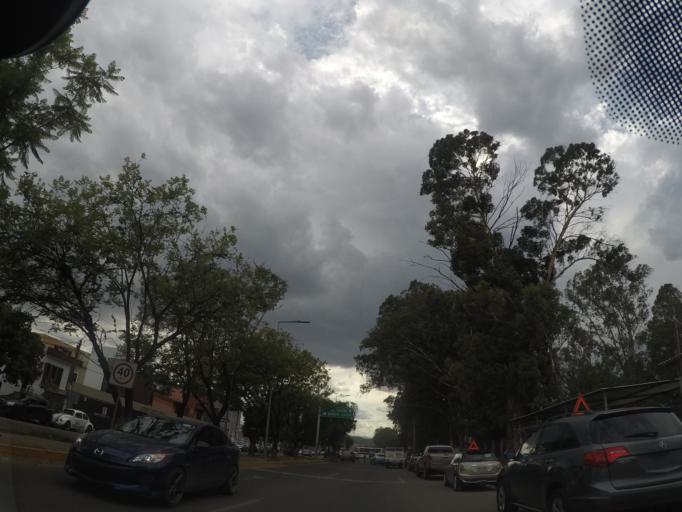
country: MX
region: Oaxaca
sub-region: Santa Cruz Amilpas
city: Santa Cruz Amilpas
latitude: 17.0688
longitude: -96.6935
